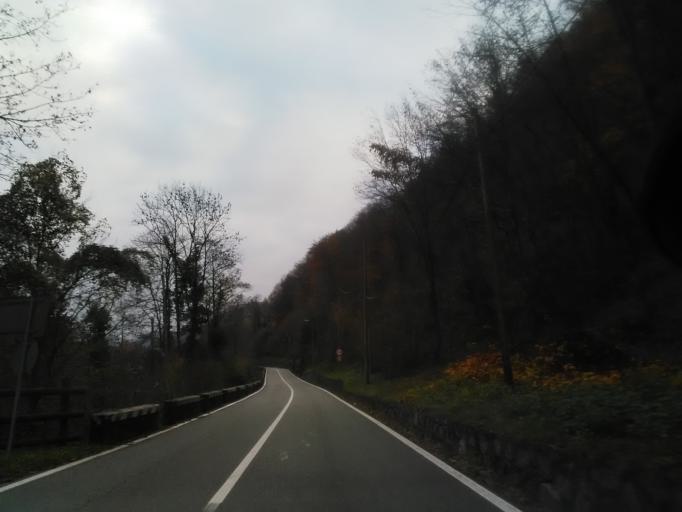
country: IT
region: Piedmont
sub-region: Provincia di Vercelli
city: Varallo
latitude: 45.8242
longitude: 8.2478
